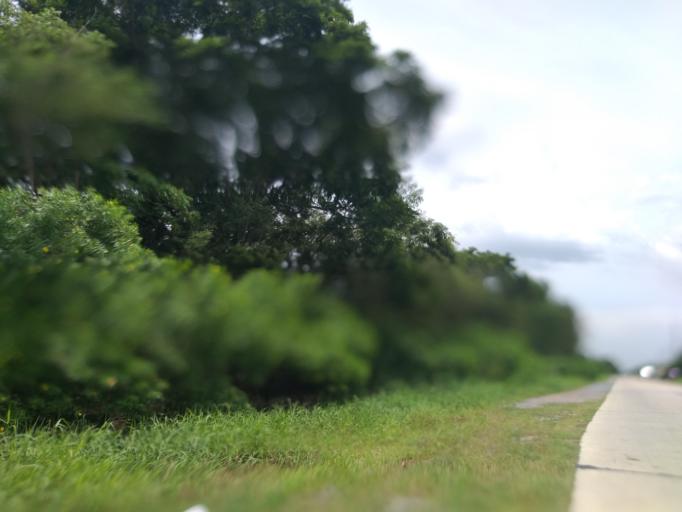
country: TH
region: Pathum Thani
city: Ban Lam Luk Ka
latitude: 13.9995
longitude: 100.8446
